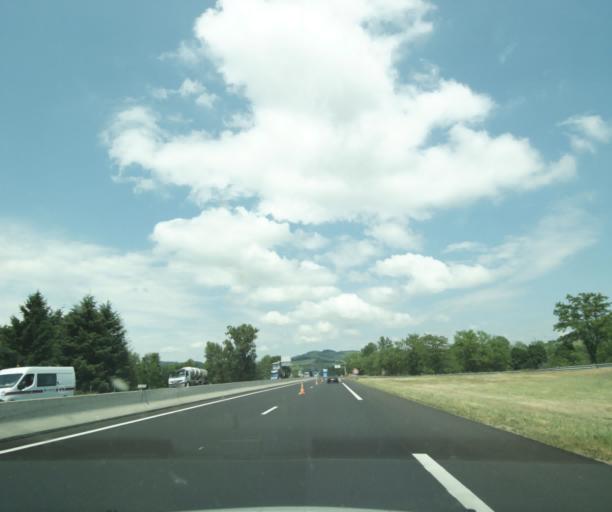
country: FR
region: Auvergne
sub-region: Departement du Puy-de-Dome
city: Issoire
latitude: 45.5433
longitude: 3.2677
